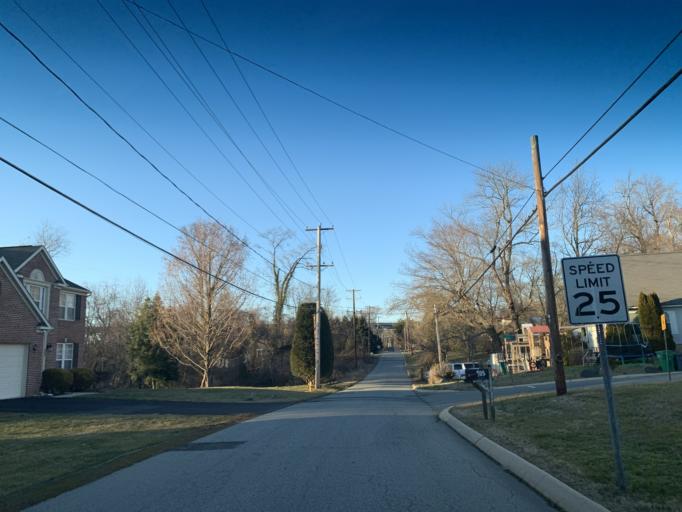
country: US
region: Maryland
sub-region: Cecil County
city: Perryville
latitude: 39.5629
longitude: -76.0778
